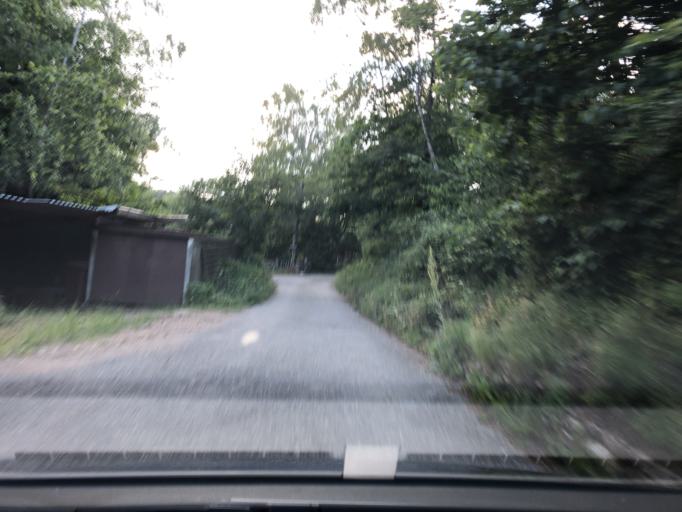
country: DE
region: Hesse
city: Unter-Abtsteinach
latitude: 49.5056
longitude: 8.7720
